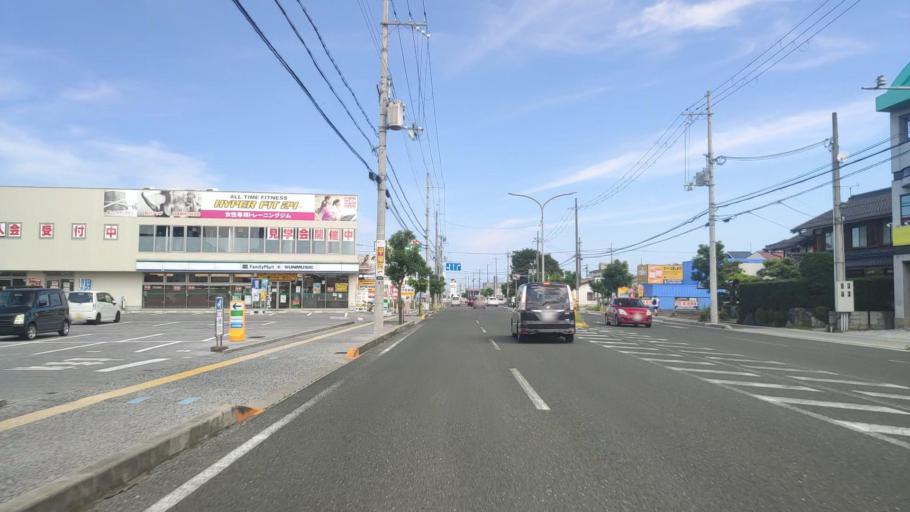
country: JP
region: Shiga Prefecture
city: Hikone
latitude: 35.2531
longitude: 136.2411
